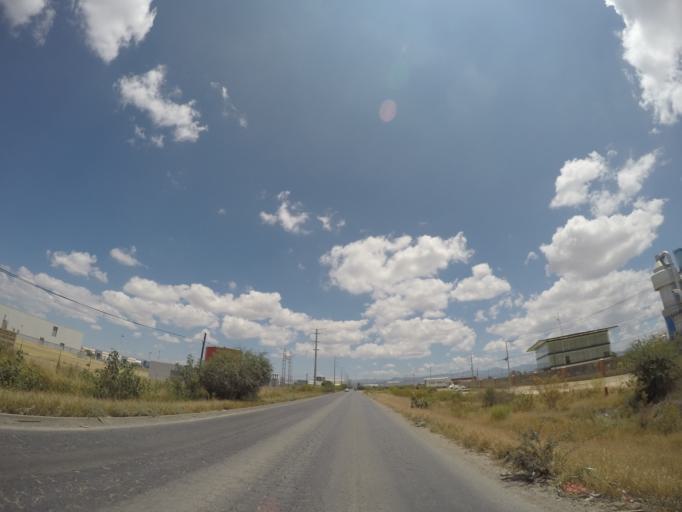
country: MX
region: San Luis Potosi
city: La Pila
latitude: 22.0445
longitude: -100.8796
